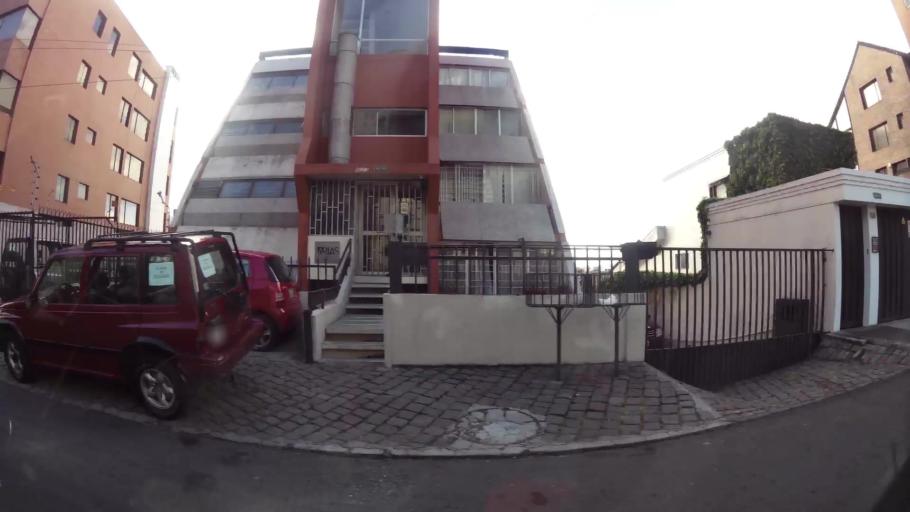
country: EC
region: Pichincha
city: Quito
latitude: -0.1930
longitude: -78.4774
